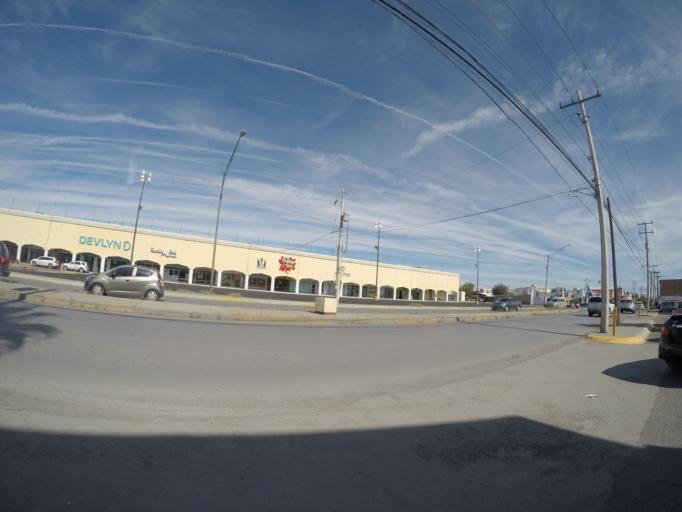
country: MX
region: Chihuahua
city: Ciudad Juarez
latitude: 31.7334
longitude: -106.4457
